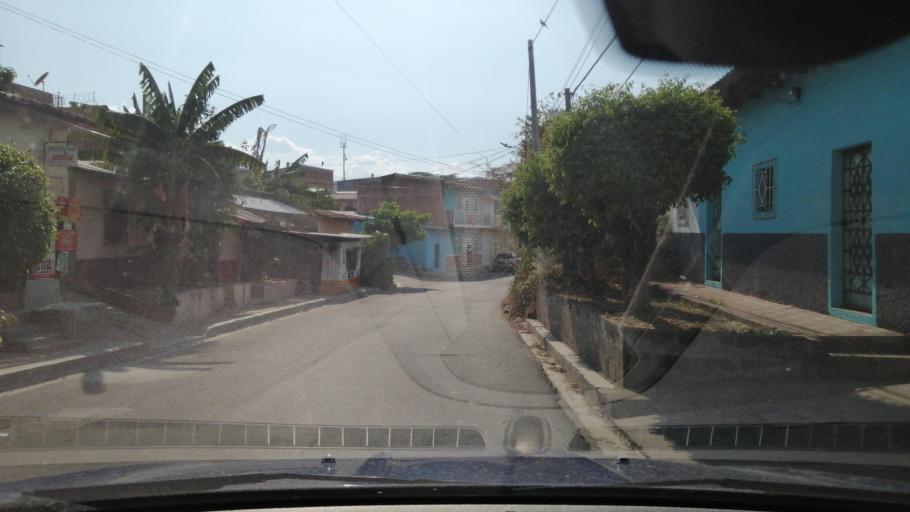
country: SV
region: Santa Ana
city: Metapan
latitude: 14.3301
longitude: -89.4381
